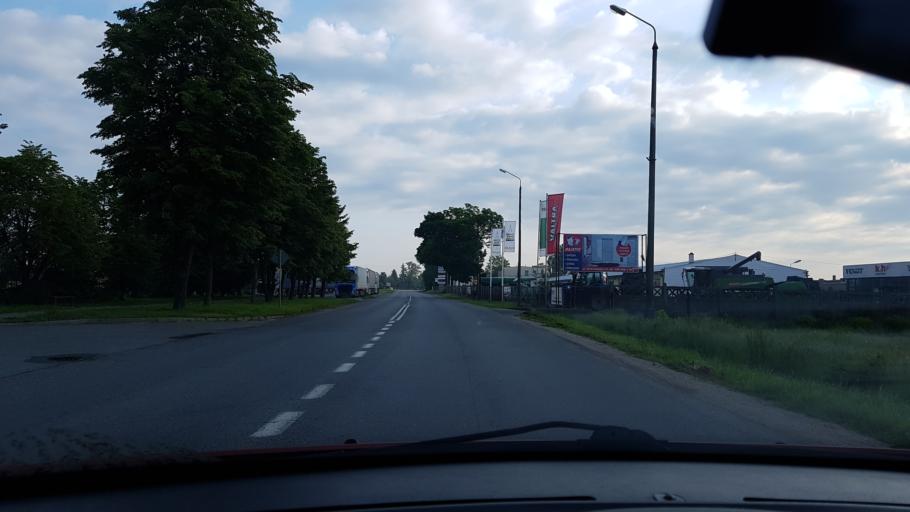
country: PL
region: Lower Silesian Voivodeship
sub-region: Powiat zabkowicki
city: Zabkowice Slaskie
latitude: 50.5998
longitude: 16.8192
